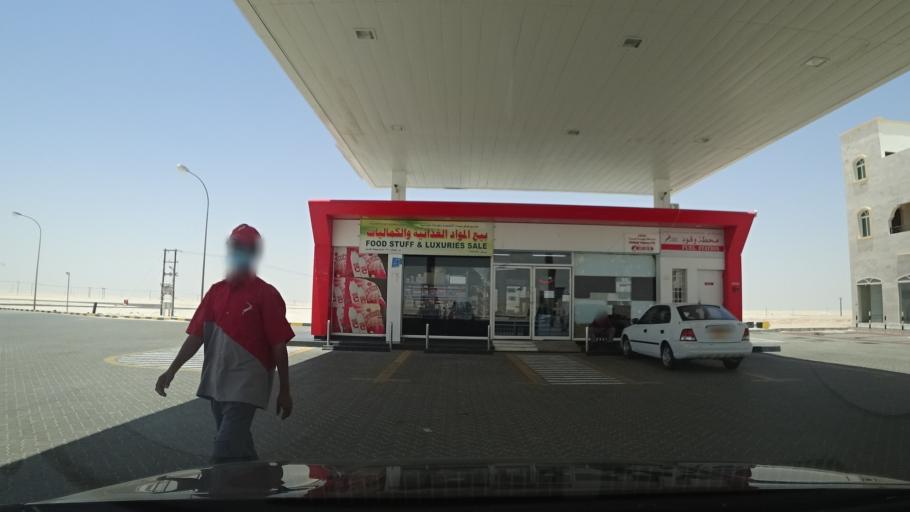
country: OM
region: Al Wusta
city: Hayma'
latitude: 19.9277
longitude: 56.2140
